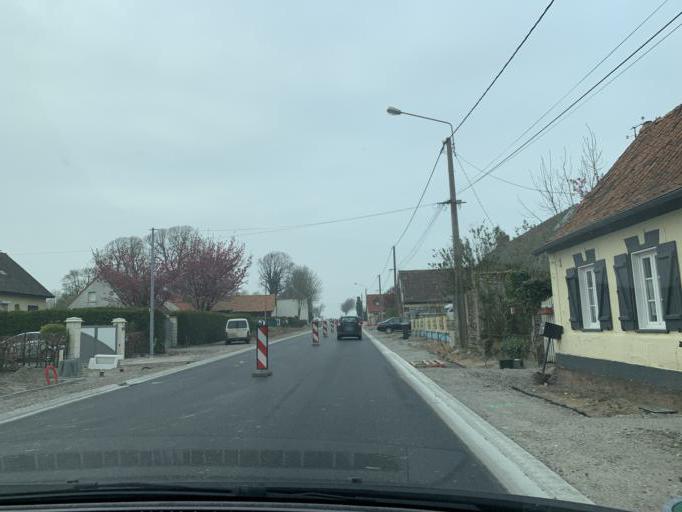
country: FR
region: Nord-Pas-de-Calais
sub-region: Departement du Pas-de-Calais
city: Montreuil
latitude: 50.4174
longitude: 1.7268
